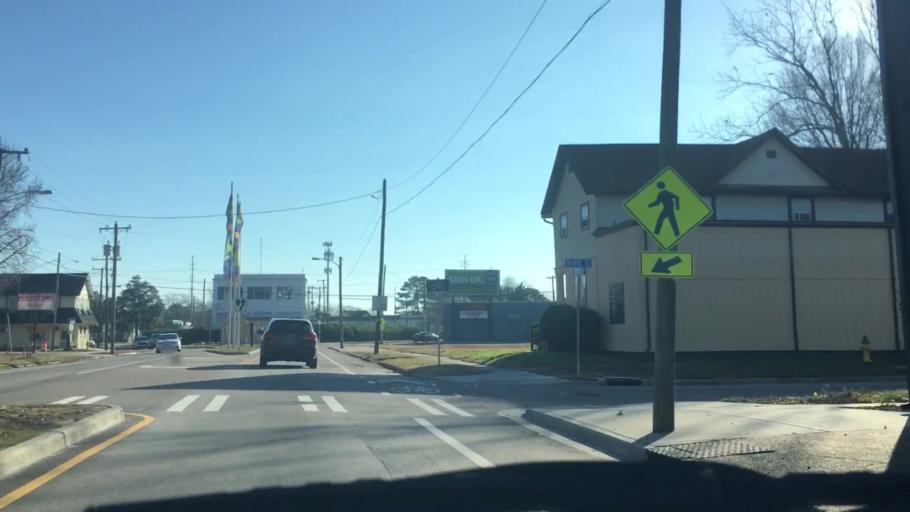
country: US
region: Virginia
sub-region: City of Norfolk
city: Norfolk
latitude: 36.8756
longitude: -76.2552
